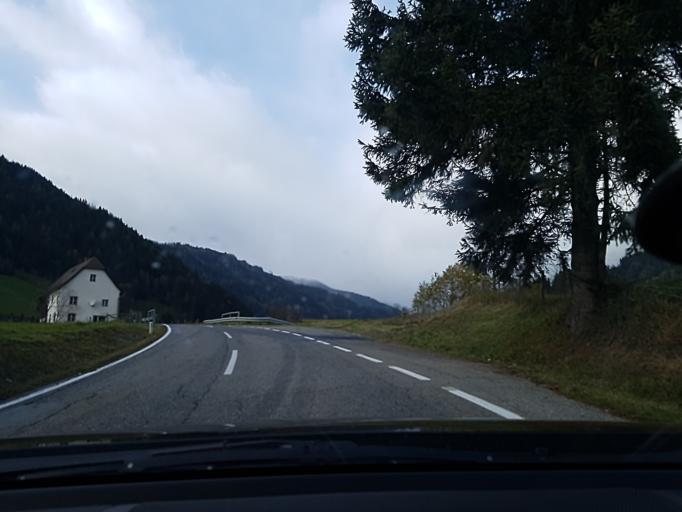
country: AT
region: Styria
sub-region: Politischer Bezirk Murtal
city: Sankt Johann am Tauern
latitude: 47.3114
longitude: 14.4852
